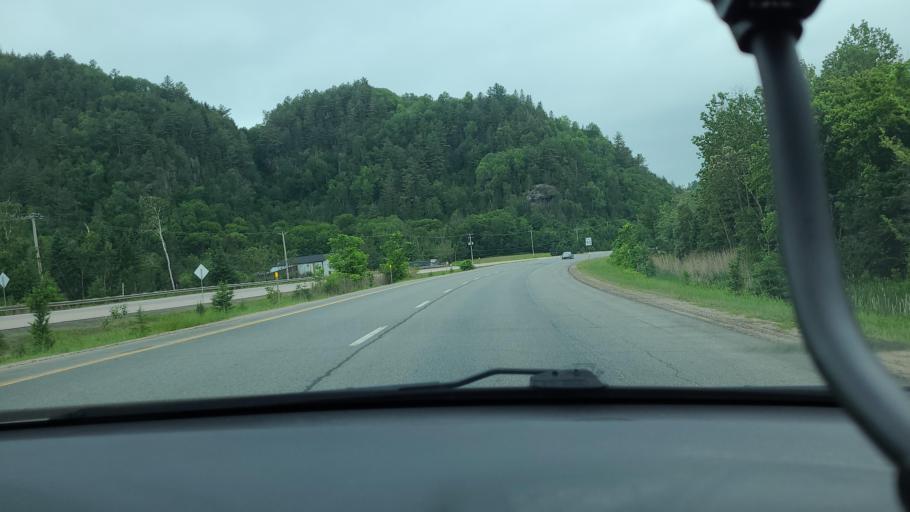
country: CA
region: Quebec
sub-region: Laurentides
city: Labelle
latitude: 46.1574
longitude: -74.7020
